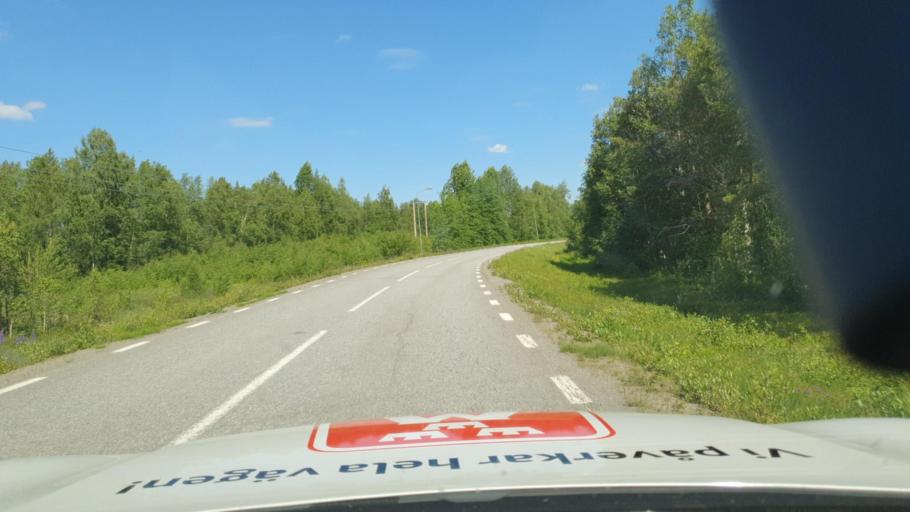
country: SE
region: Vaesterbotten
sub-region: Skelleftea Kommun
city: Boliden
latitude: 64.8426
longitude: 20.3688
